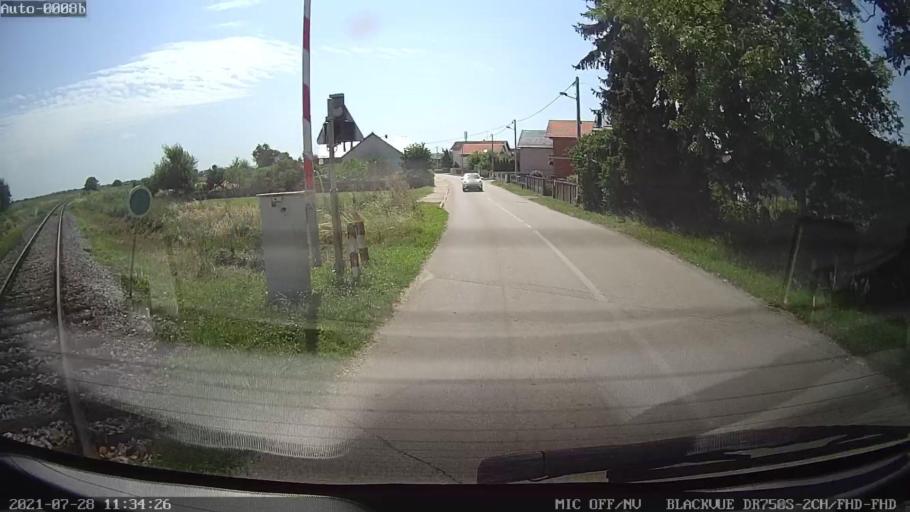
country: HR
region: Varazdinska
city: Varazdin
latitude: 46.2907
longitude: 16.3765
